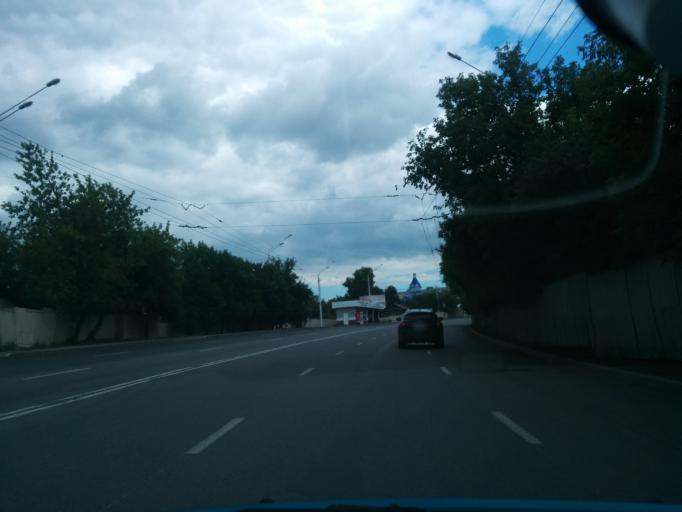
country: RU
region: Bashkortostan
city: Ufa
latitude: 54.7227
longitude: 55.9757
